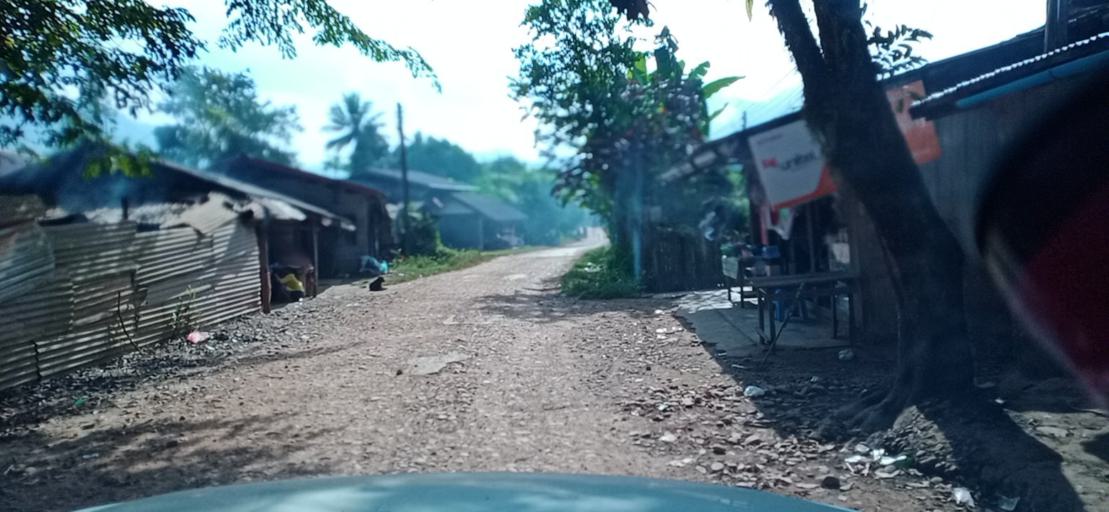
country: TH
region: Changwat Bueng Kan
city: Pak Khat
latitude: 18.6774
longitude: 103.1919
